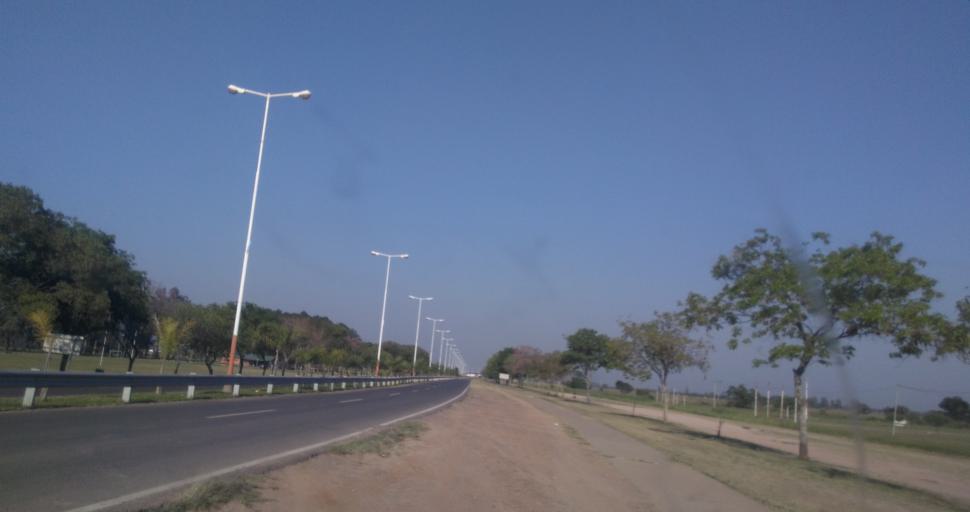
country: AR
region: Chaco
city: Fontana
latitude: -27.4406
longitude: -59.0324
